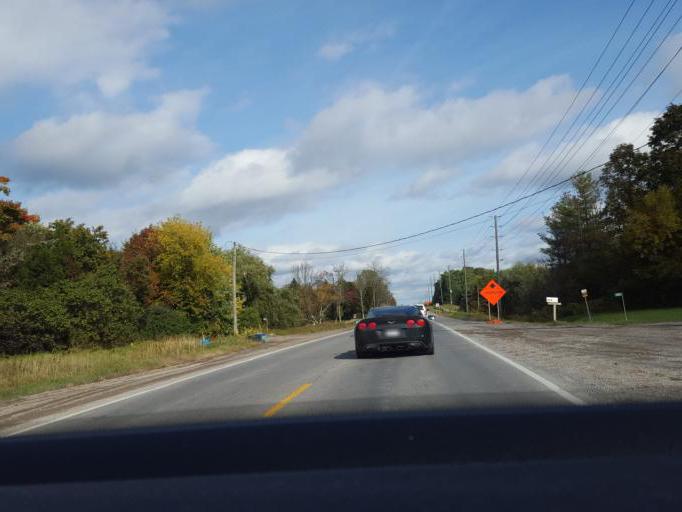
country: CA
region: Ontario
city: Oshawa
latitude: 43.9570
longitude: -78.7739
